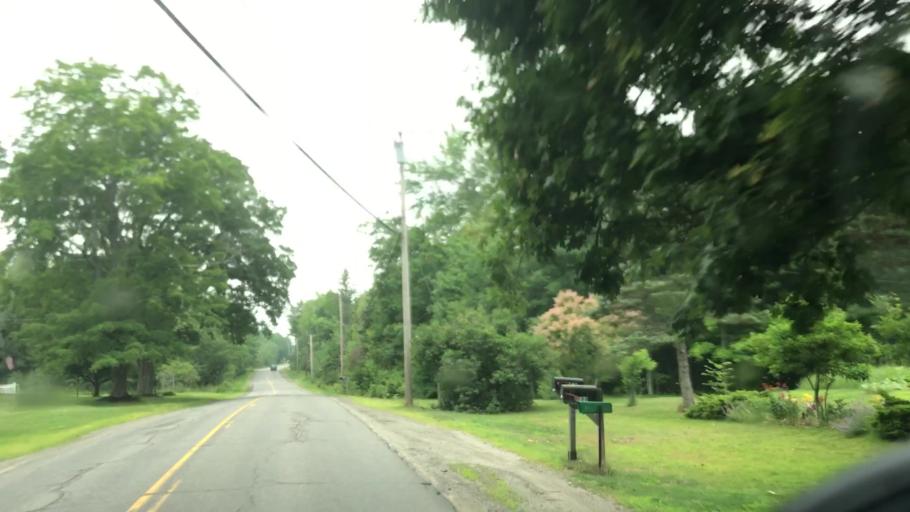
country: US
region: Maine
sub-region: Penobscot County
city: Orono
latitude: 44.8850
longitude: -68.7083
